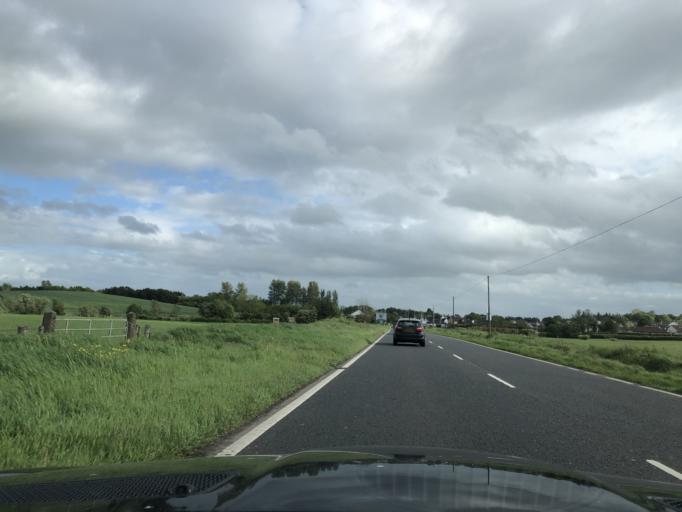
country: GB
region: Northern Ireland
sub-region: Ballymoney District
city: Ballymoney
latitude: 55.0844
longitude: -6.5275
